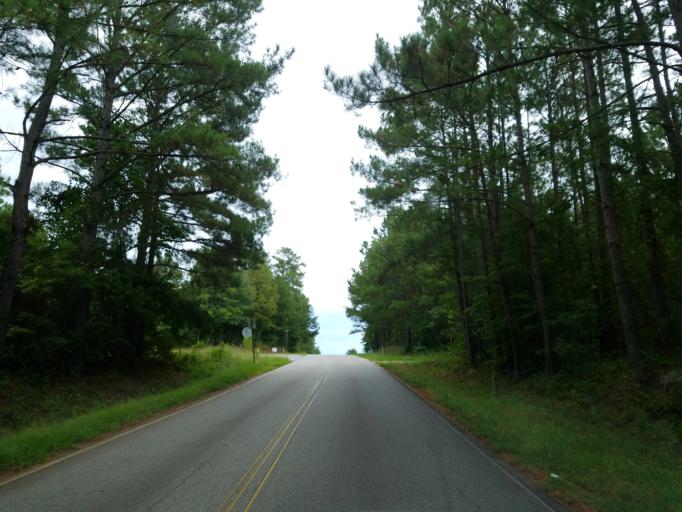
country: US
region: Georgia
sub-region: Bibb County
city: West Point
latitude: 32.9056
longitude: -83.8599
